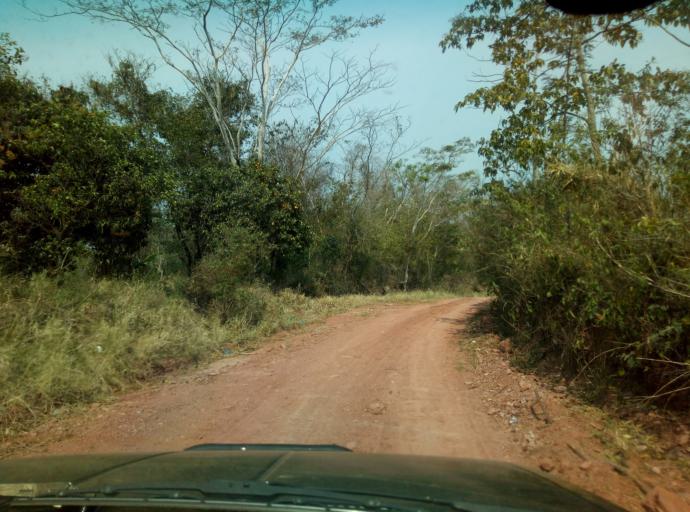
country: PY
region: Caaguazu
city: Yhu
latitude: -25.1758
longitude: -56.0896
